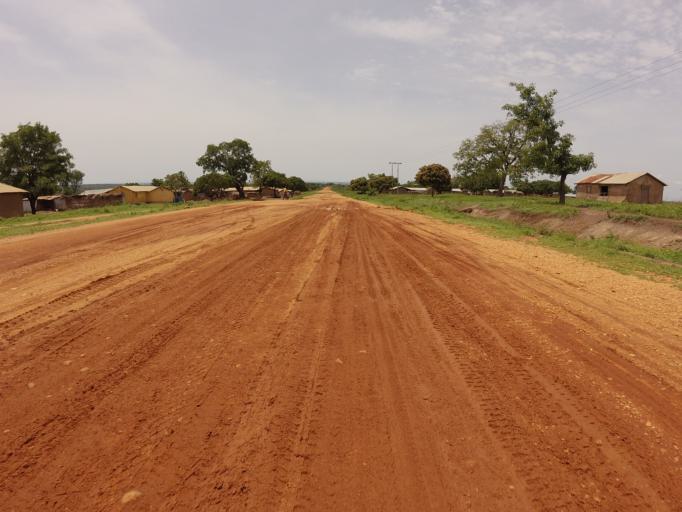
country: GH
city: Kpandae
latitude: 8.7345
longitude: 0.0936
